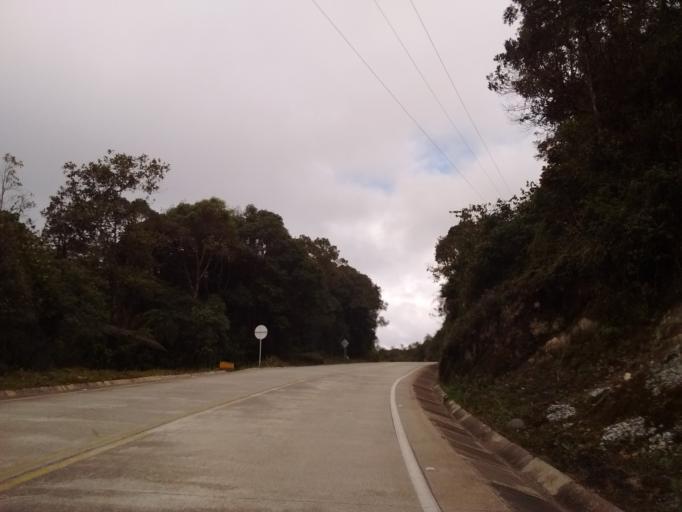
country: CO
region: Huila
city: Isnos
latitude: 2.0504
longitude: -76.3124
